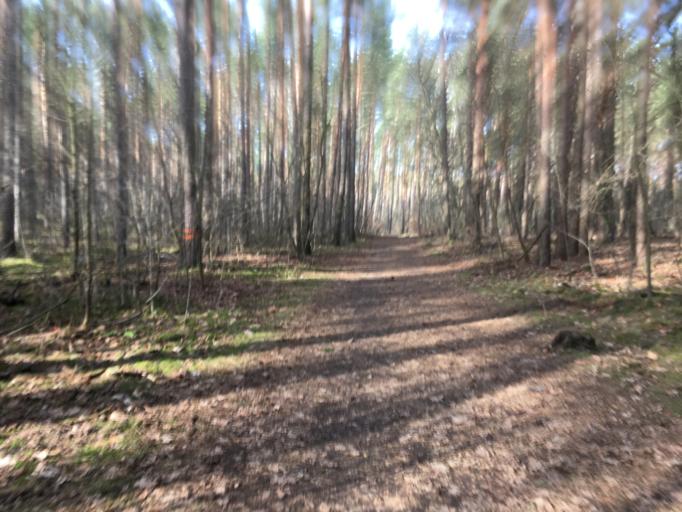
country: DE
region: Brandenburg
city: Bernau bei Berlin
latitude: 52.6876
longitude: 13.5403
